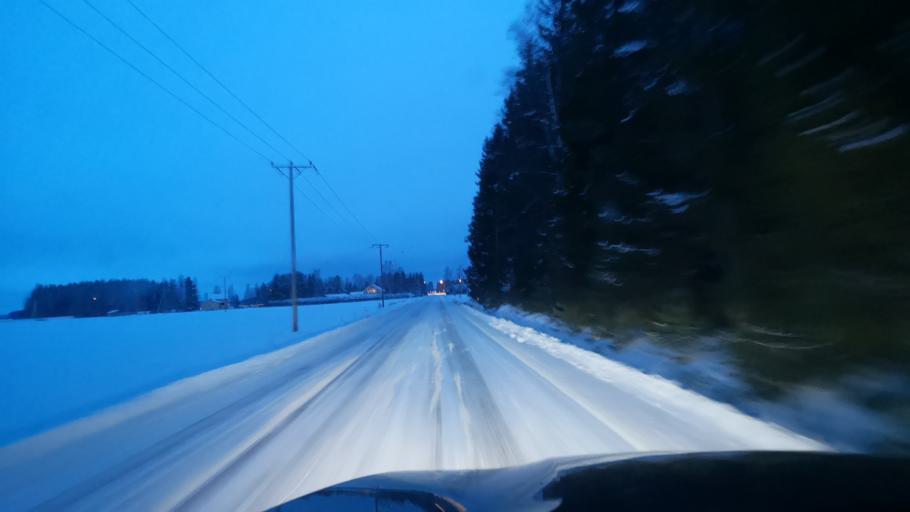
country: FI
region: Varsinais-Suomi
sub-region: Loimaa
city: Loimaa
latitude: 60.8794
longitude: 23.0895
